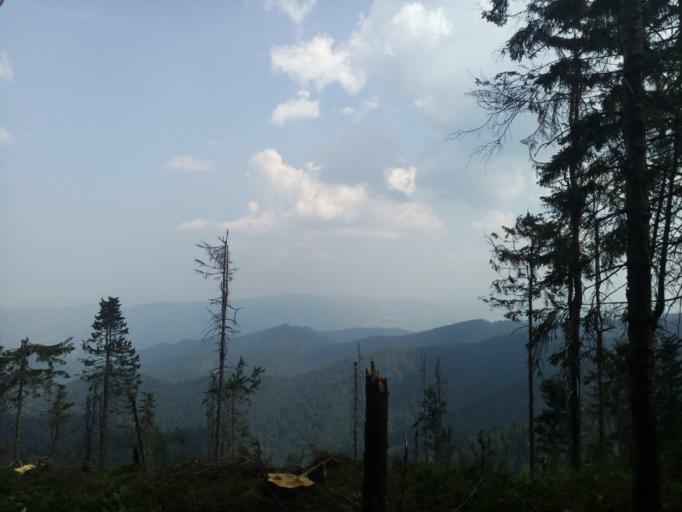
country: PL
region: Lesser Poland Voivodeship
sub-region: Powiat nowosadecki
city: Rytro
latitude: 49.4612
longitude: 20.5781
